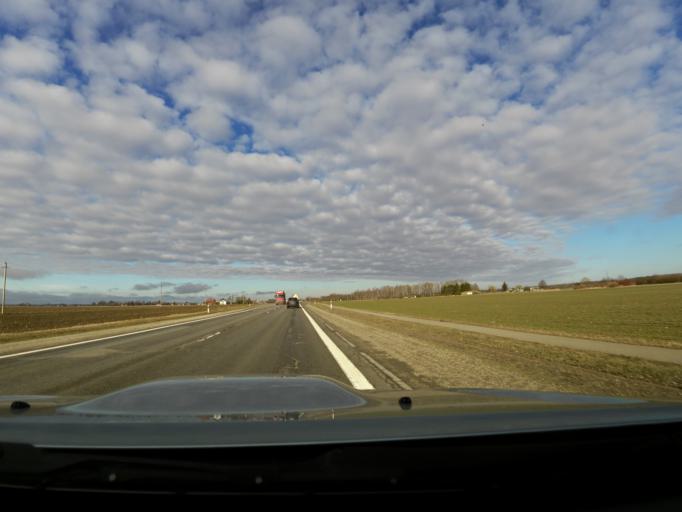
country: LT
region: Panevezys
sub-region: Panevezys City
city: Panevezys
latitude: 55.7390
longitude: 24.1957
